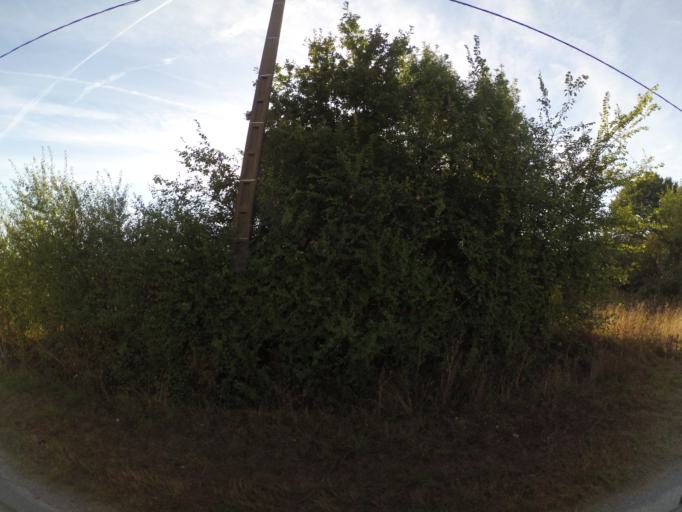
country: FR
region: Pays de la Loire
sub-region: Departement de la Loire-Atlantique
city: Vieillevigne
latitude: 46.9764
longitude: -1.4100
